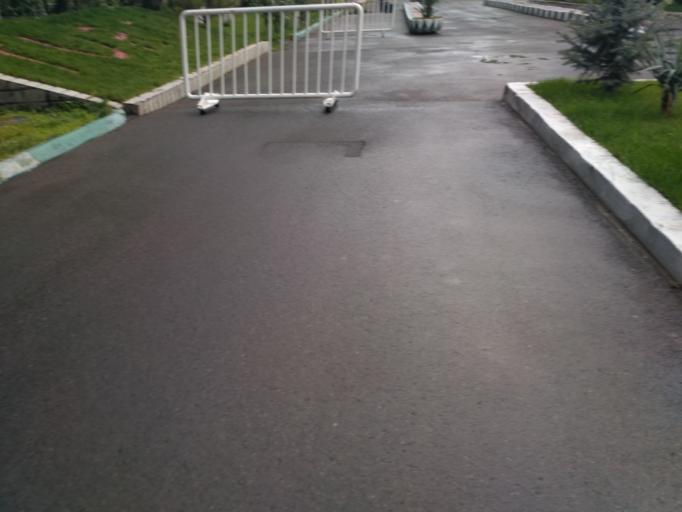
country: UZ
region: Toshkent
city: Salor
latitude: 41.3434
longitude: 69.3575
